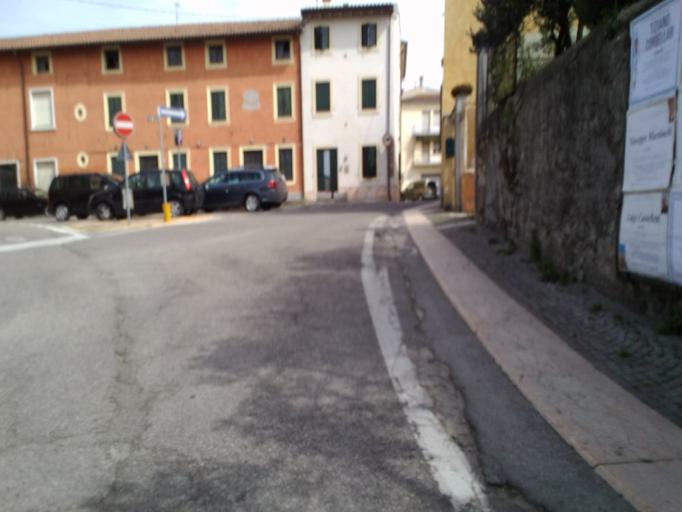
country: IT
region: Veneto
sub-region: Provincia di Verona
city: Sommacampagna
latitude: 45.4066
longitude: 10.8420
